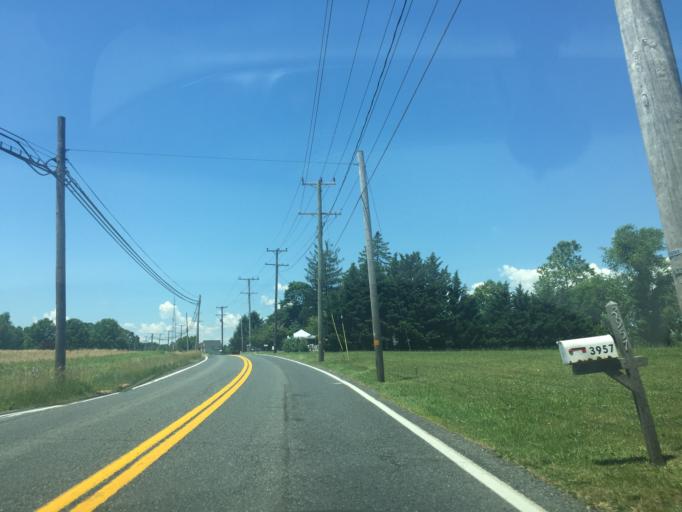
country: US
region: Maryland
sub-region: Harford County
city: Jarrettsville
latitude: 39.6117
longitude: -76.5022
